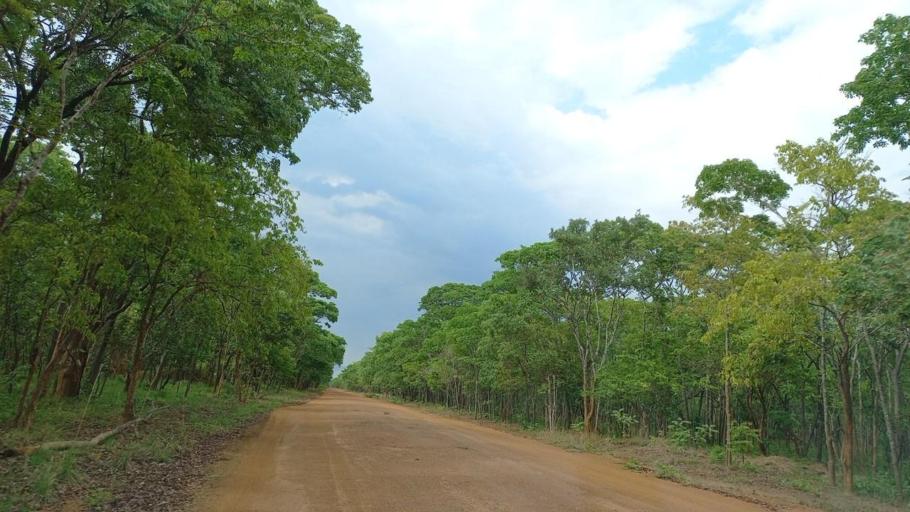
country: ZM
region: North-Western
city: Kalengwa
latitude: -13.3952
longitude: 25.0689
